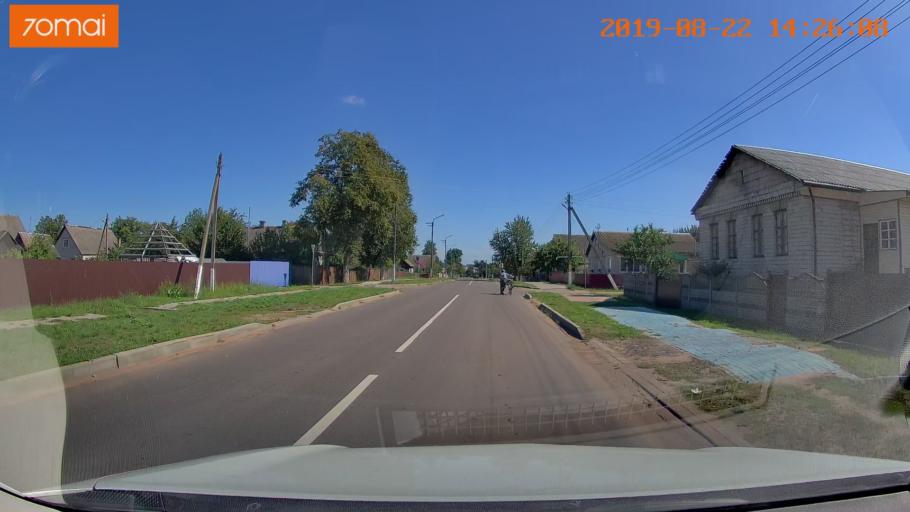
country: BY
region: Mogilev
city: Asipovichy
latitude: 53.2998
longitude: 28.6138
